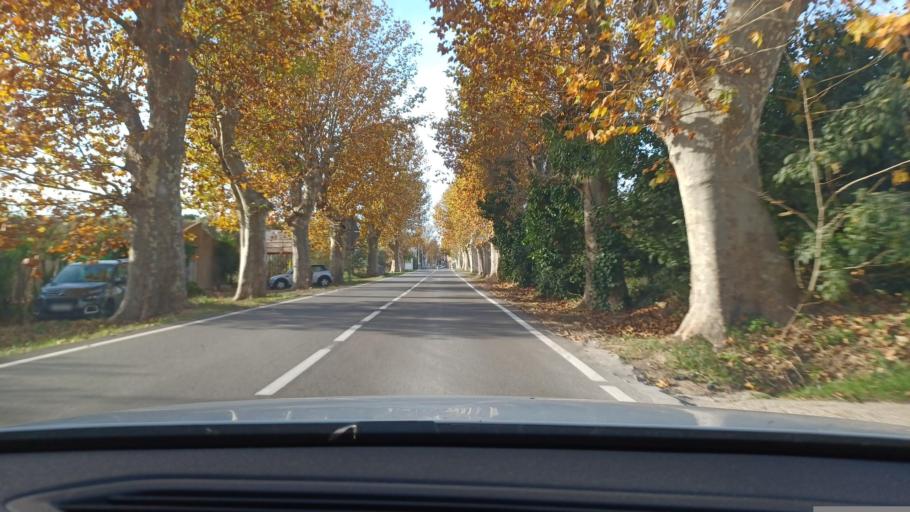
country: ES
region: Catalonia
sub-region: Provincia de Tarragona
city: Ulldecona
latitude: 40.6017
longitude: 0.4526
